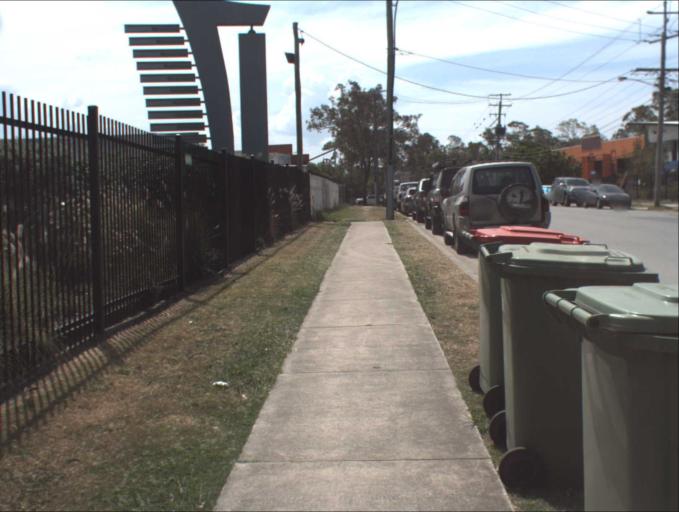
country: AU
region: Queensland
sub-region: Logan
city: Beenleigh
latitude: -27.6759
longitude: 153.1881
